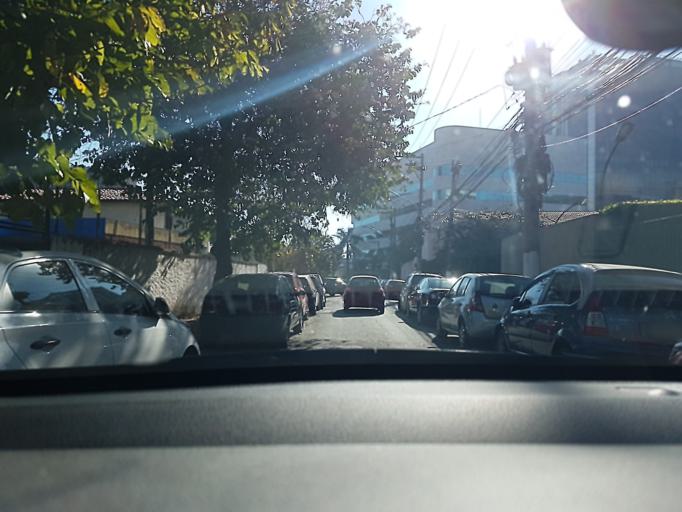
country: BR
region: Sao Paulo
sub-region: Taboao Da Serra
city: Taboao da Serra
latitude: -23.6323
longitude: -46.7126
